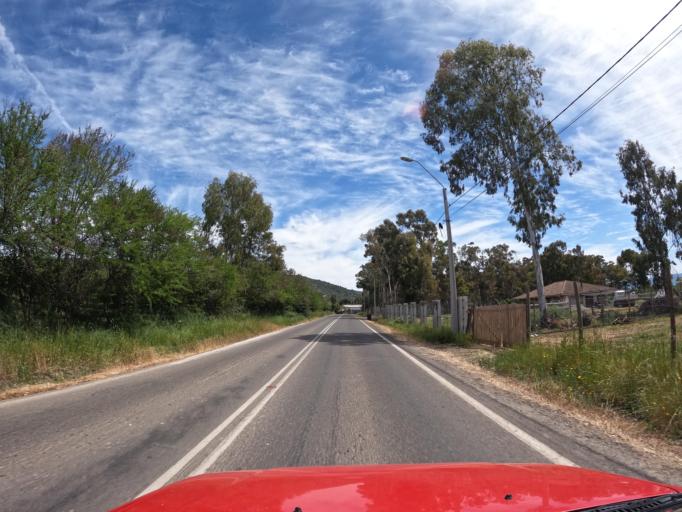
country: CL
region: Maule
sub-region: Provincia de Talca
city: Talca
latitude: -35.1173
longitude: -71.6433
